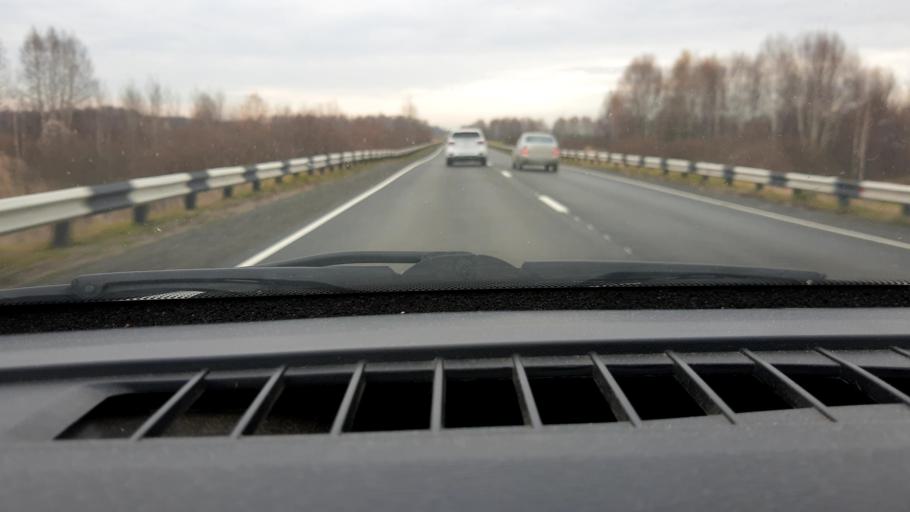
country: RU
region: Nizjnij Novgorod
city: Novaya Balakhna
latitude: 56.5856
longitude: 43.6748
